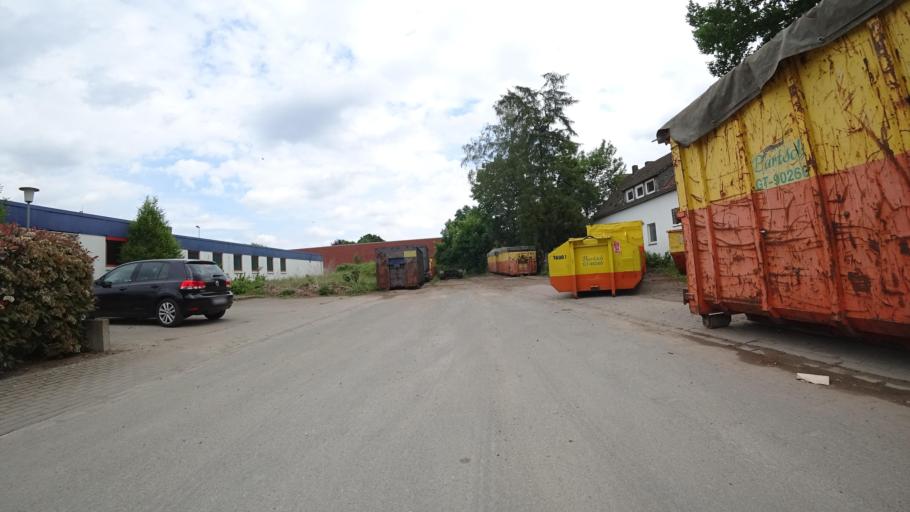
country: DE
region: North Rhine-Westphalia
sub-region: Regierungsbezirk Detmold
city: Guetersloh
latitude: 51.9090
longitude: 8.4038
